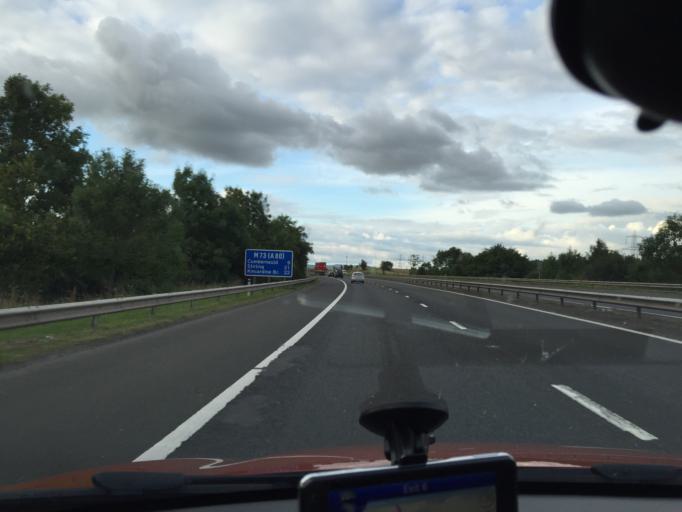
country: GB
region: Scotland
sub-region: North Lanarkshire
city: Glenboig
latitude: 55.8956
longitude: -4.0690
